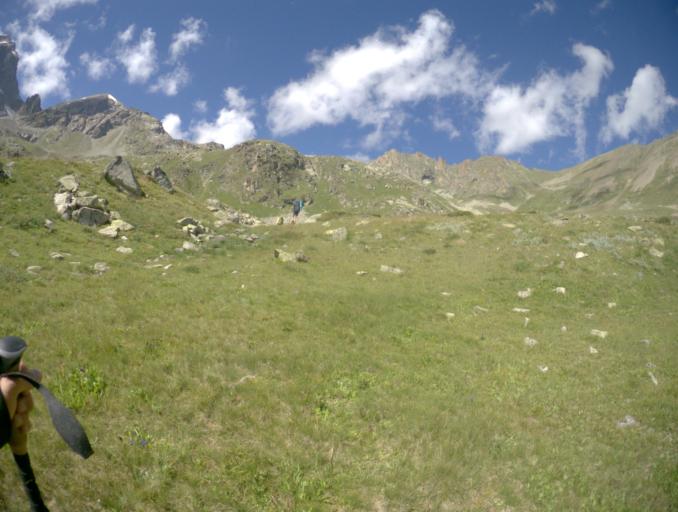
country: RU
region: Karachayevo-Cherkesiya
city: Uchkulan
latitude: 43.3248
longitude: 42.1010
